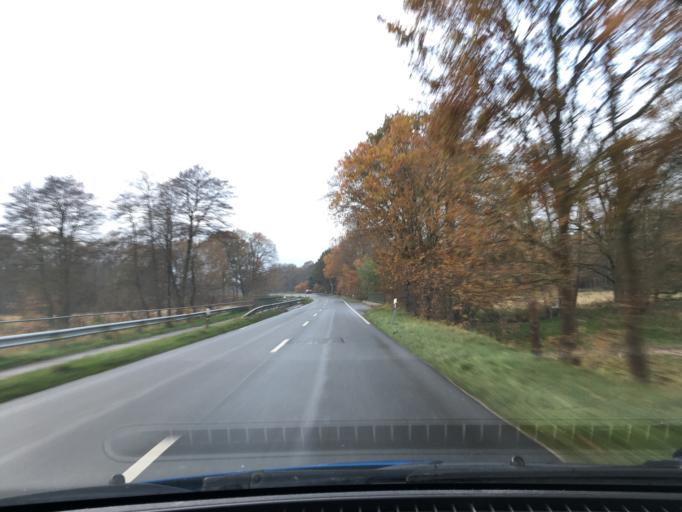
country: DE
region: Lower Saxony
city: Oldendorf
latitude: 53.1776
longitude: 10.2192
